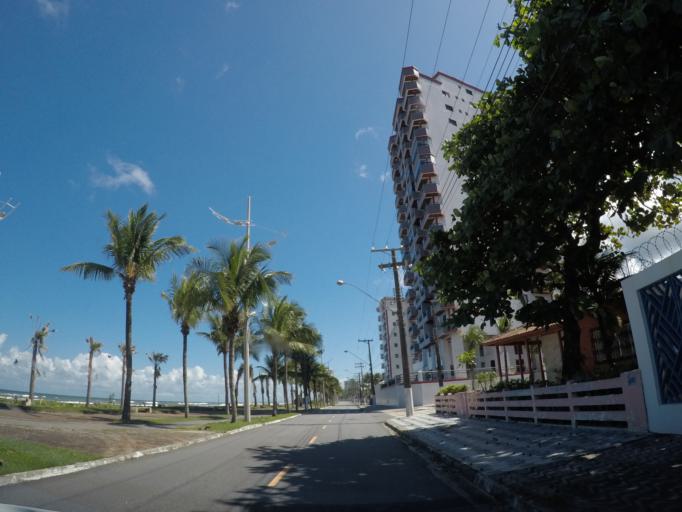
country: BR
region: Sao Paulo
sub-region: Mongagua
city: Mongagua
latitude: -24.0805
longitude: -46.5885
